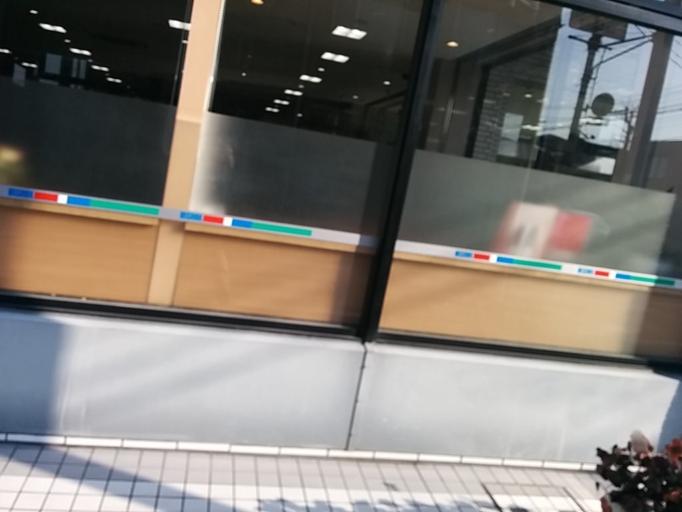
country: JP
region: Saitama
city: Kawagoe
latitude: 35.9186
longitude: 139.4779
